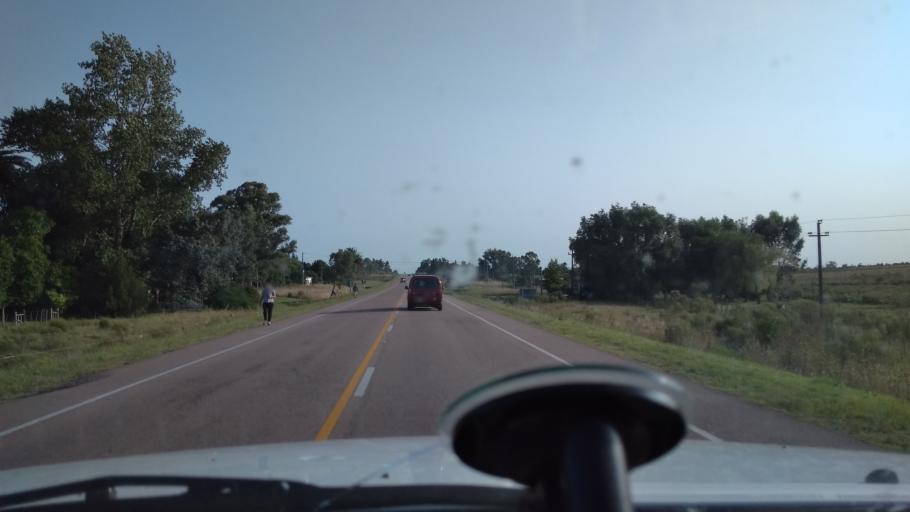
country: UY
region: Canelones
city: Sauce
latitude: -34.6164
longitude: -56.0494
